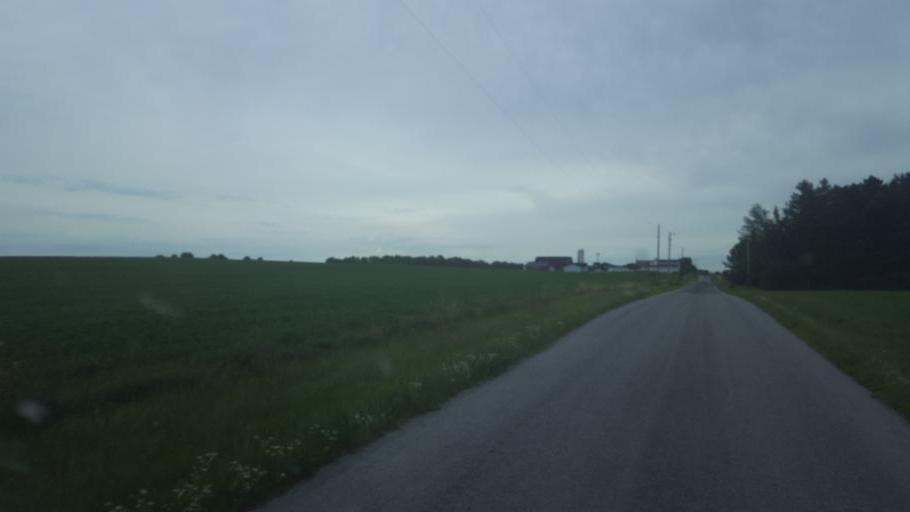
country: US
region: Ohio
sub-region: Huron County
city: Greenwich
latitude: 40.9240
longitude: -82.4873
